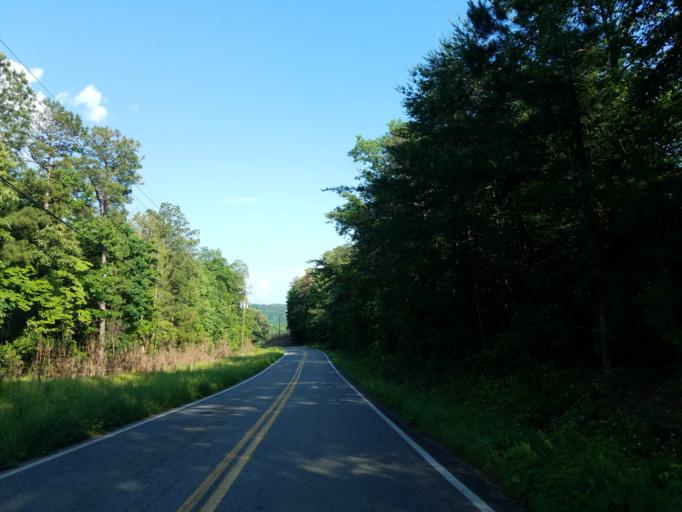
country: US
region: Georgia
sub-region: Pickens County
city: Nelson
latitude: 34.3781
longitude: -84.3595
